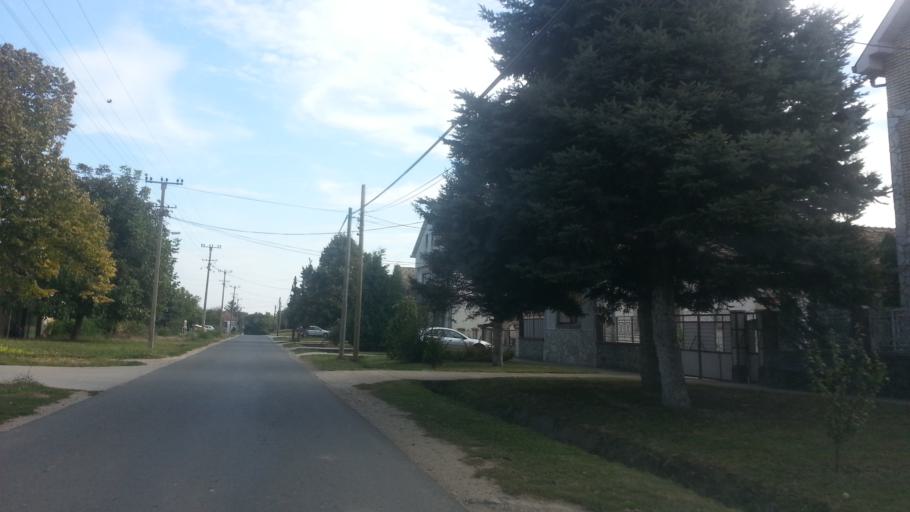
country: RS
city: Belegis
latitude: 45.0158
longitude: 20.3224
